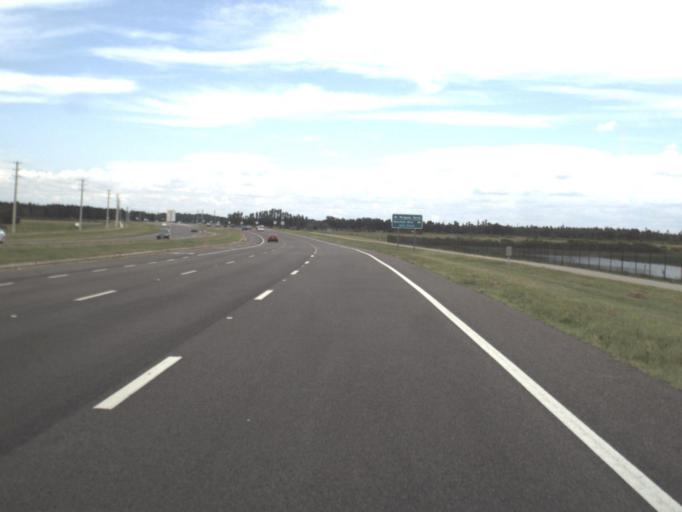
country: US
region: Florida
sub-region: Hillsborough County
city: Pebble Creek
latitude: 28.1926
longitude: -82.3367
